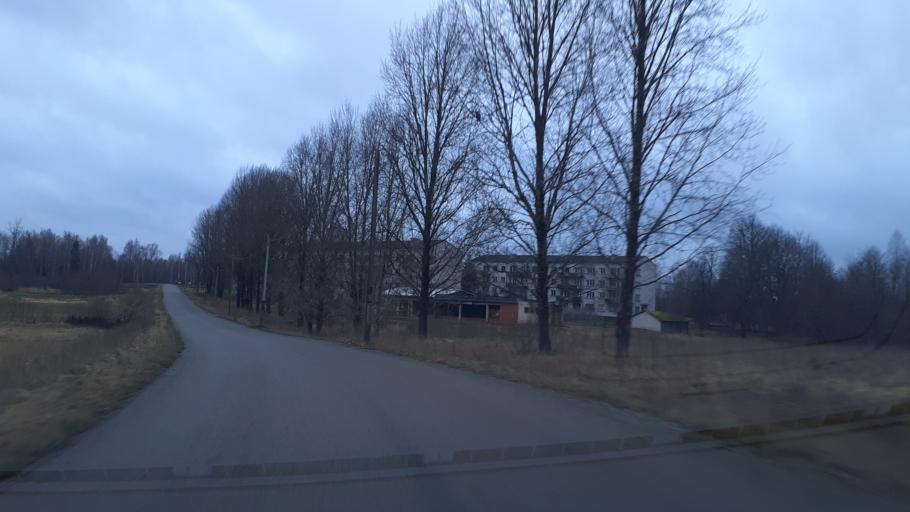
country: LV
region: Kuldigas Rajons
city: Kuldiga
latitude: 57.0422
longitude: 22.1297
